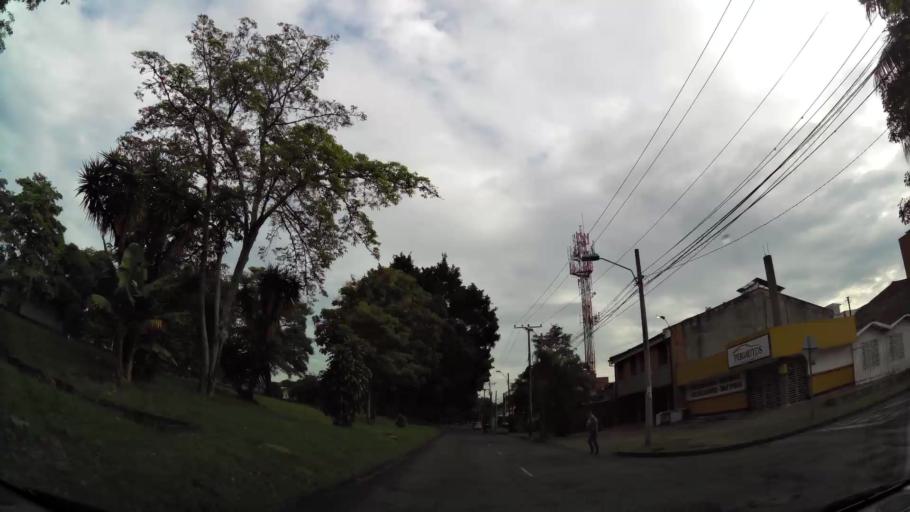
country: CO
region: Valle del Cauca
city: Cali
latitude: 3.4781
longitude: -76.5227
